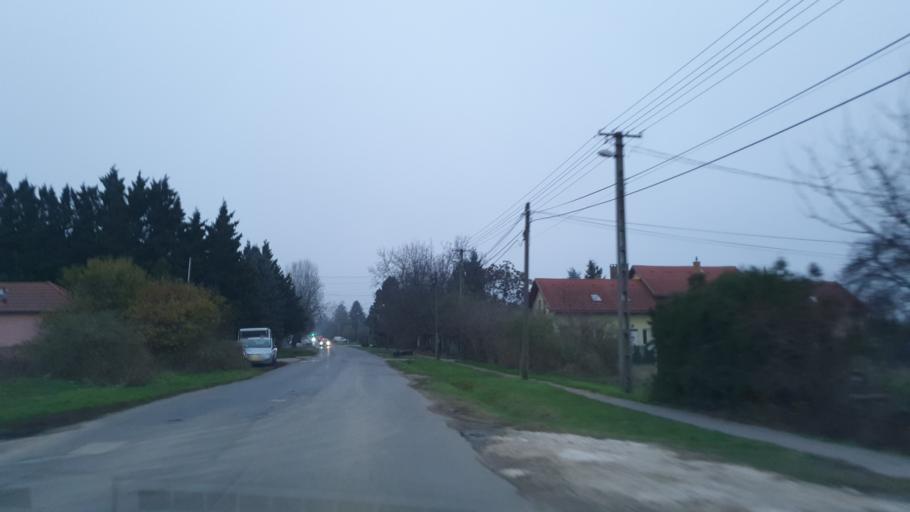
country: HU
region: Pest
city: Csomor
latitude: 47.5300
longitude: 19.2237
